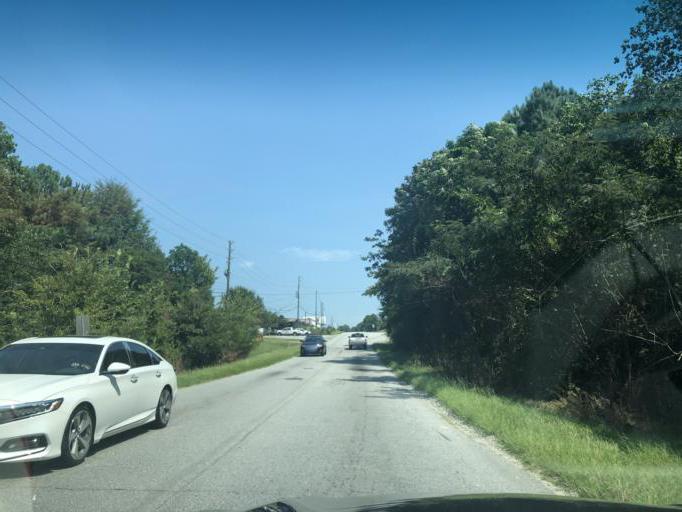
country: US
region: Georgia
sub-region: Muscogee County
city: Columbus
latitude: 32.5136
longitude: -84.9208
